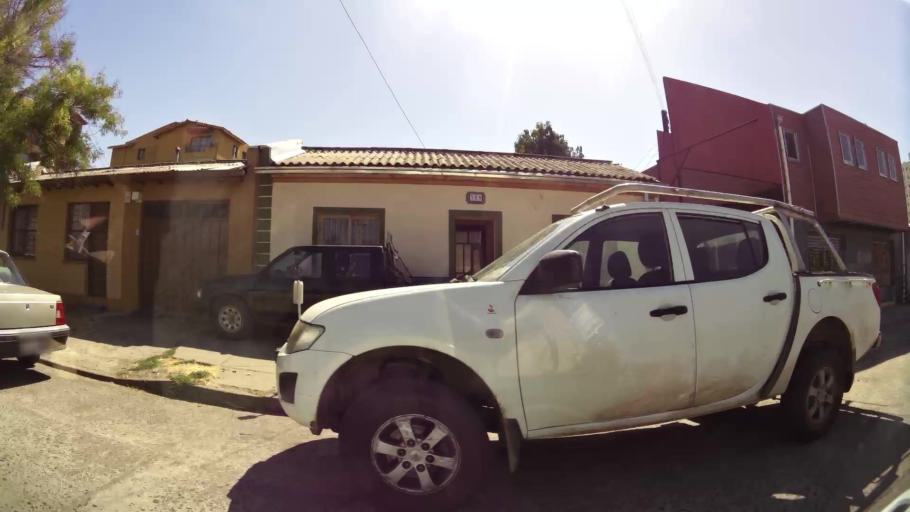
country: CL
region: Maule
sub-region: Provincia de Talca
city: Talca
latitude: -35.4316
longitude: -71.6602
